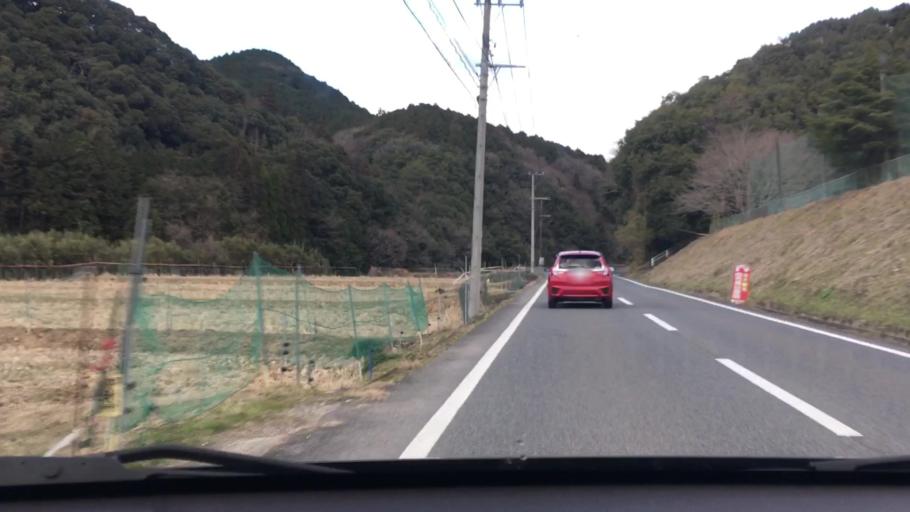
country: JP
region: Oita
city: Bungo-Takada-shi
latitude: 33.4514
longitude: 131.3928
